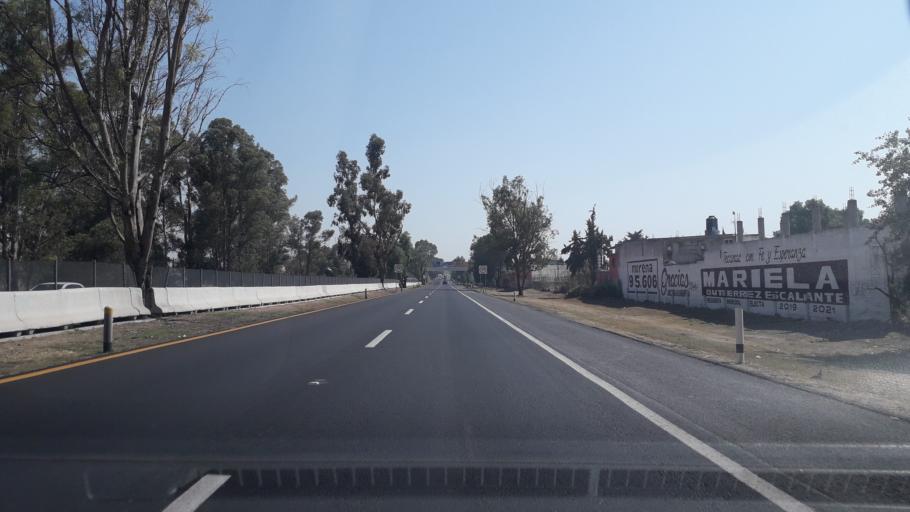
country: MX
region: Mexico
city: Santo Tomas Chiconautla
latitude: 19.6404
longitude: -99.0180
